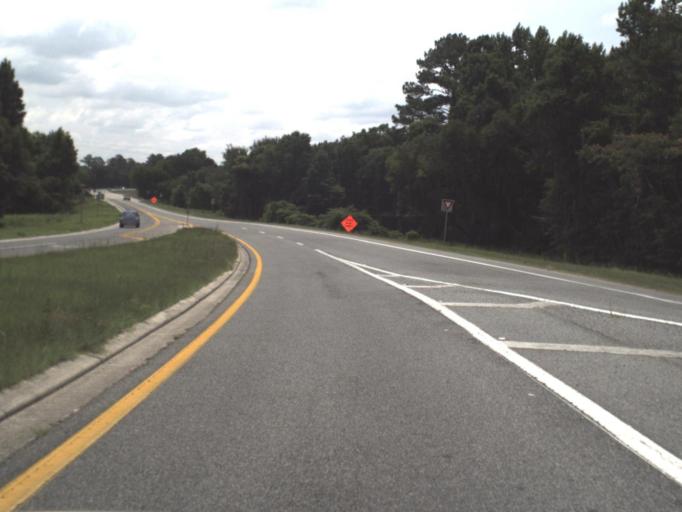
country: US
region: Florida
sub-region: Hamilton County
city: Jasper
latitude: 30.5297
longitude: -83.0419
